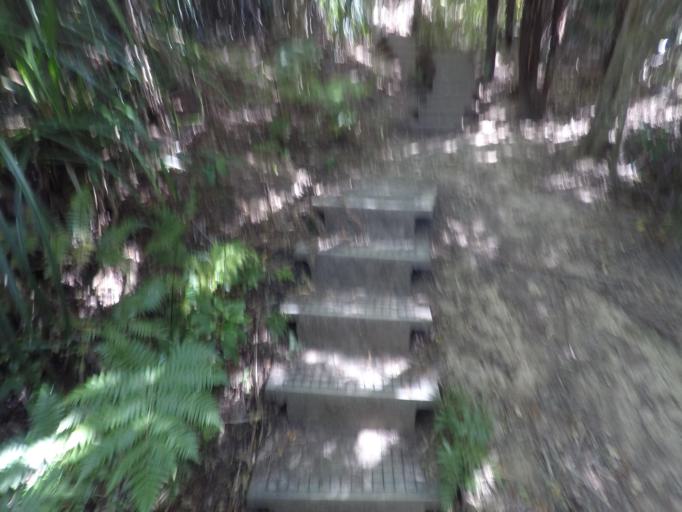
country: NZ
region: Auckland
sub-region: Auckland
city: North Shore
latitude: -36.8226
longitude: 174.7071
